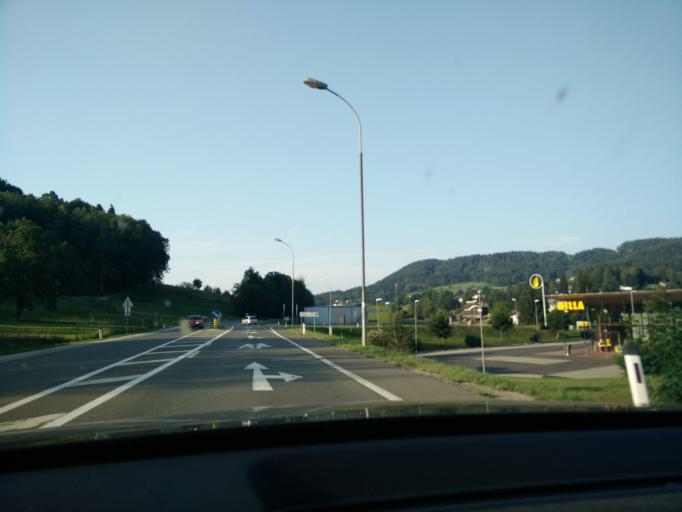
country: AT
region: Carinthia
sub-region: Politischer Bezirk Klagenfurt Land
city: Maria Rain
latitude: 46.5596
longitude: 14.2815
